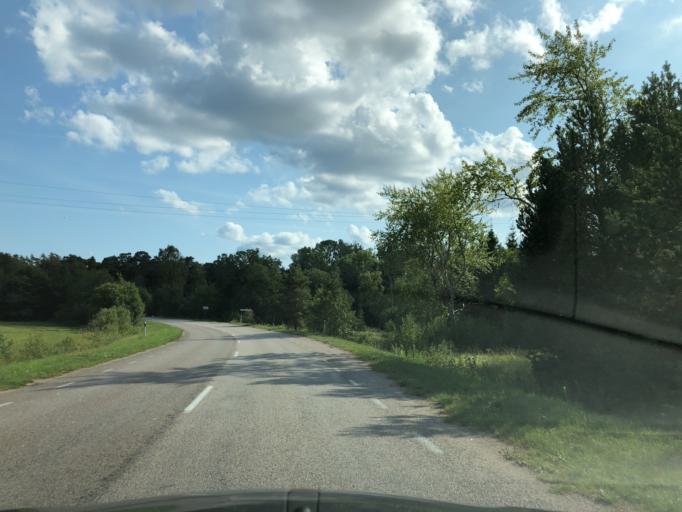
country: EE
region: Hiiumaa
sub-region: Kaerdla linn
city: Kardla
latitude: 58.7094
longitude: 22.5876
